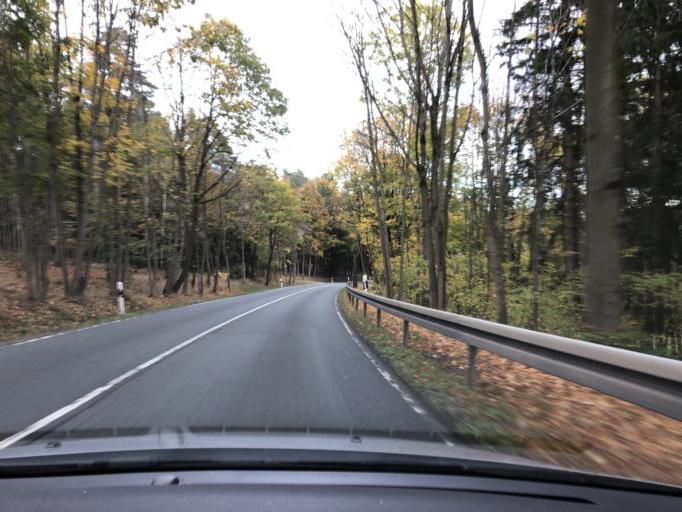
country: DE
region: Thuringia
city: Saalfeld
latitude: 50.6162
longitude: 11.3240
